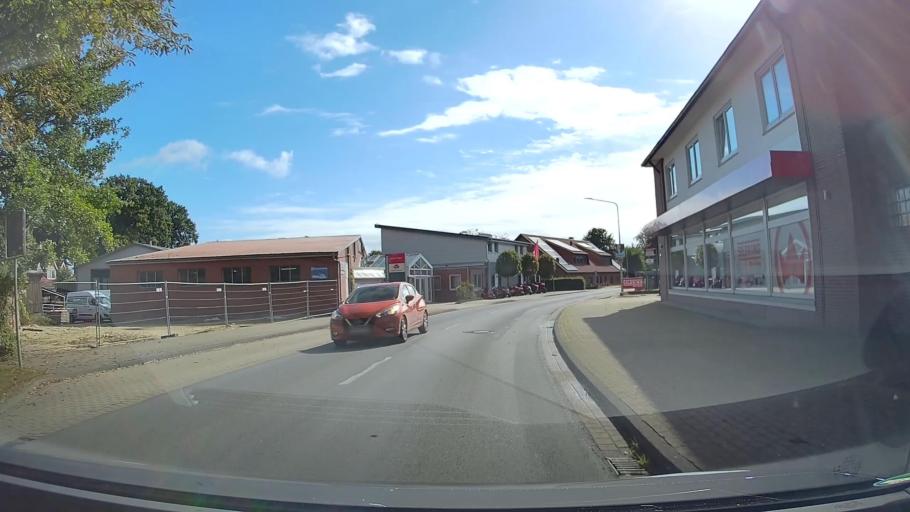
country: DE
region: Lower Saxony
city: Gnarrenburg
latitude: 53.3822
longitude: 8.9601
